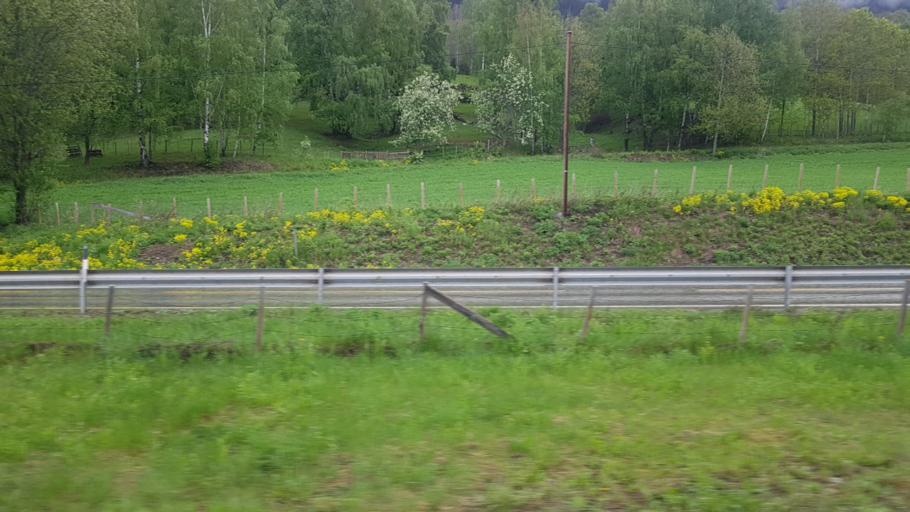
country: NO
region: Oppland
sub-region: Nord-Fron
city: Vinstra
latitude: 61.6254
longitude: 9.7169
